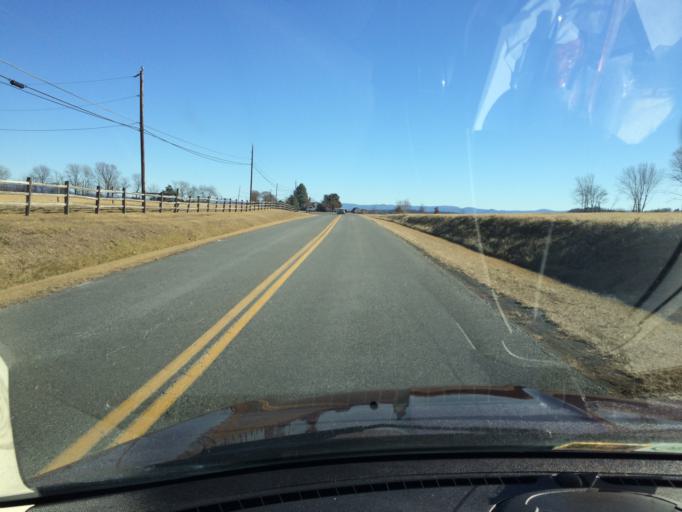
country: US
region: Virginia
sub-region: Rockingham County
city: Bridgewater
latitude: 38.3664
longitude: -78.9754
